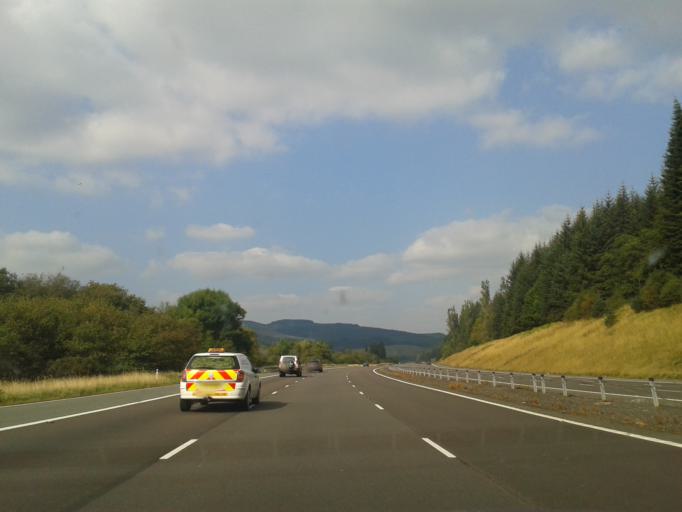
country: GB
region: Scotland
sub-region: Dumfries and Galloway
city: Moffat
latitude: 55.3473
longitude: -3.5033
